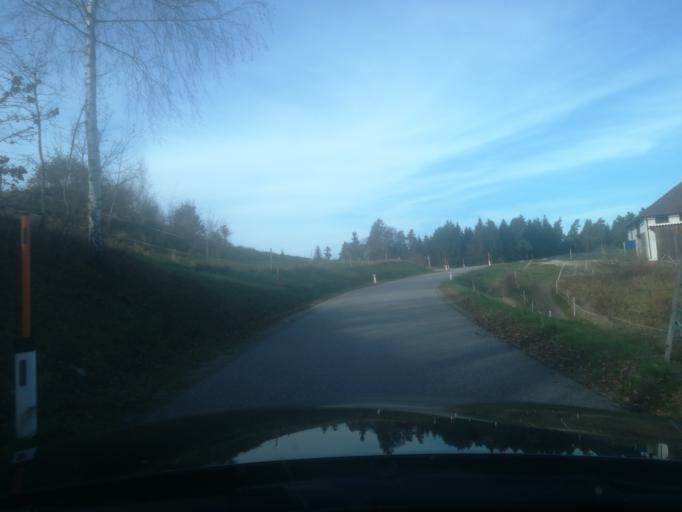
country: AT
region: Upper Austria
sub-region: Politischer Bezirk Perg
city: Perg
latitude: 48.3265
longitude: 14.6539
